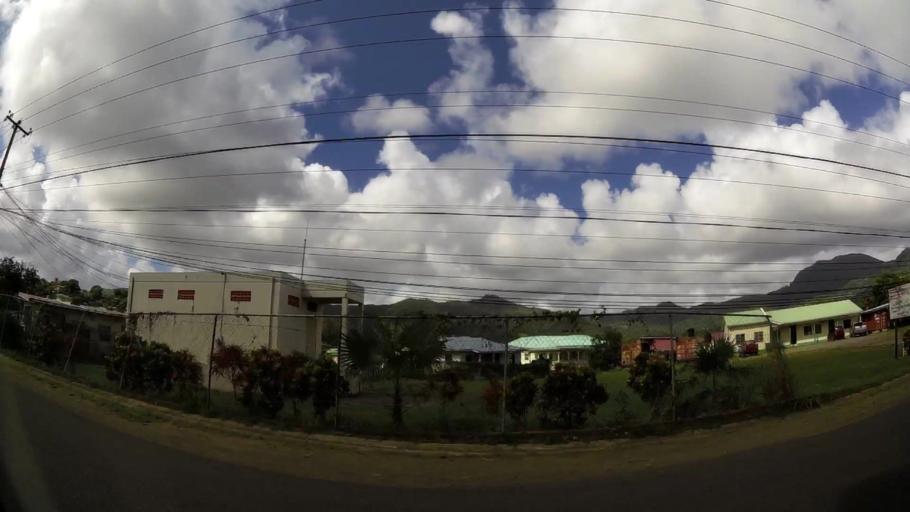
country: LC
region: Dennery Quarter
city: Dennery
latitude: 13.9356
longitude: -60.9209
